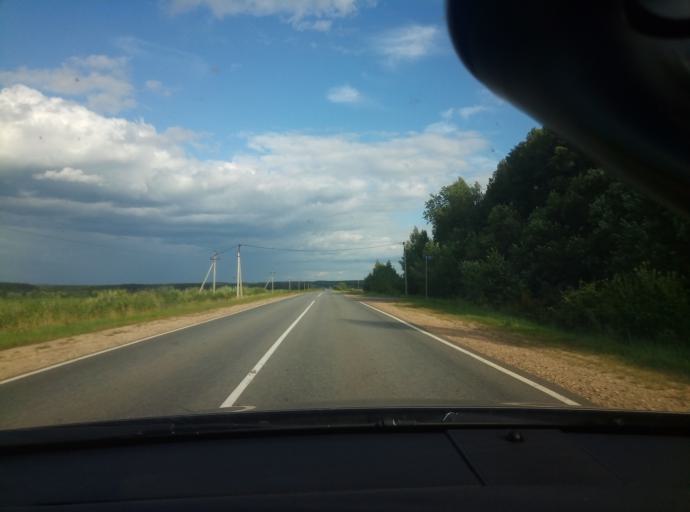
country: RU
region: Kaluga
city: Nikola-Lenivets
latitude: 54.5702
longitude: 35.4579
